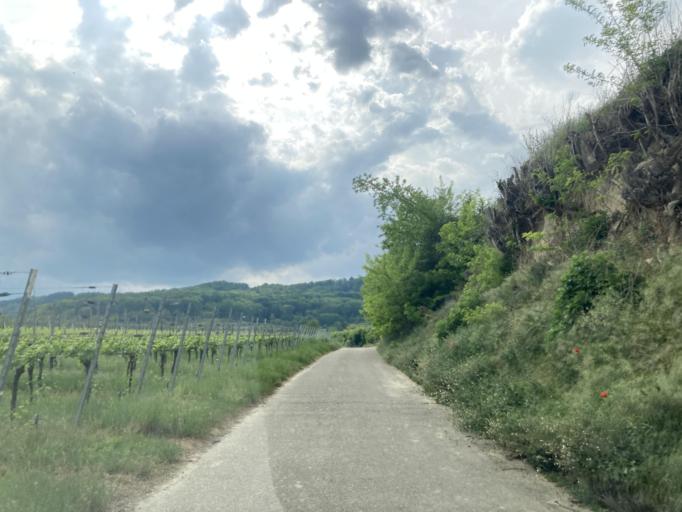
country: DE
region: Baden-Wuerttemberg
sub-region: Freiburg Region
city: Bahlingen
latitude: 48.1105
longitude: 7.7205
